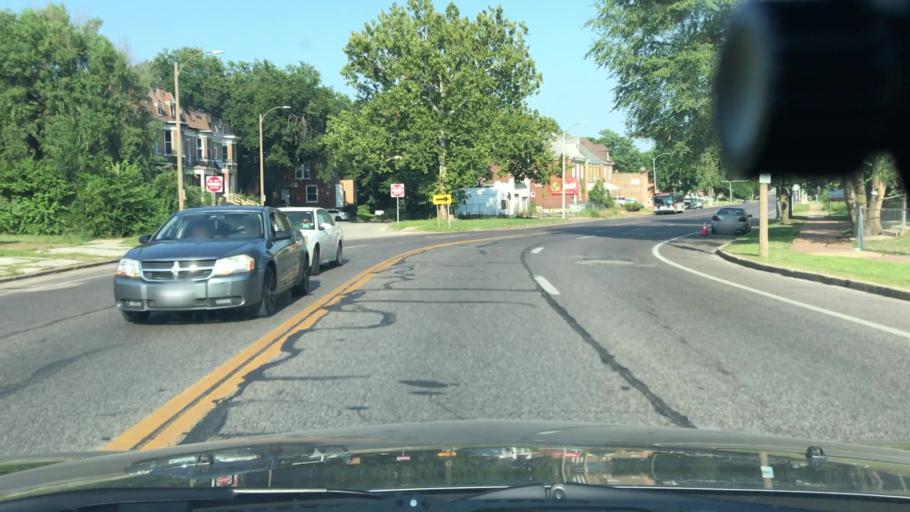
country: US
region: Missouri
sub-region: Saint Louis County
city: Hillsdale
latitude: 38.6596
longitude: -90.2587
